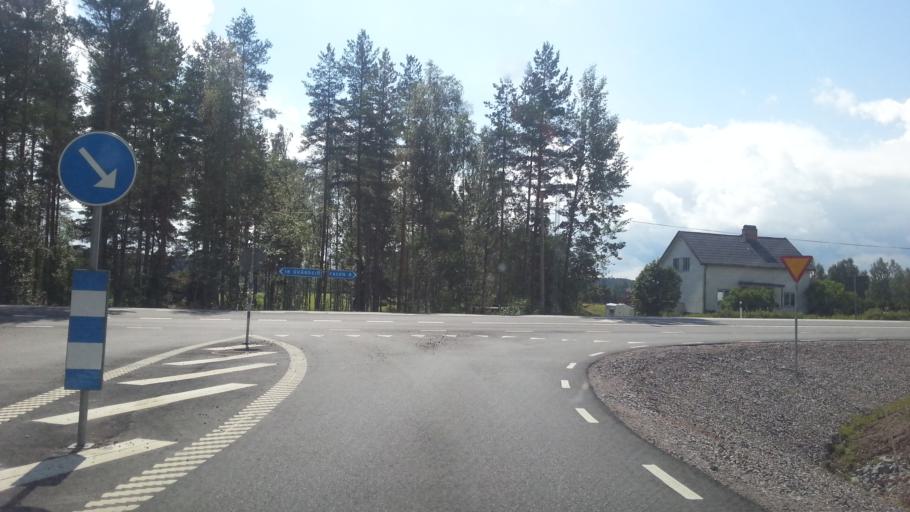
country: SE
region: Dalarna
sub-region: Faluns Kommun
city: Falun
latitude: 60.6157
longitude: 15.7637
